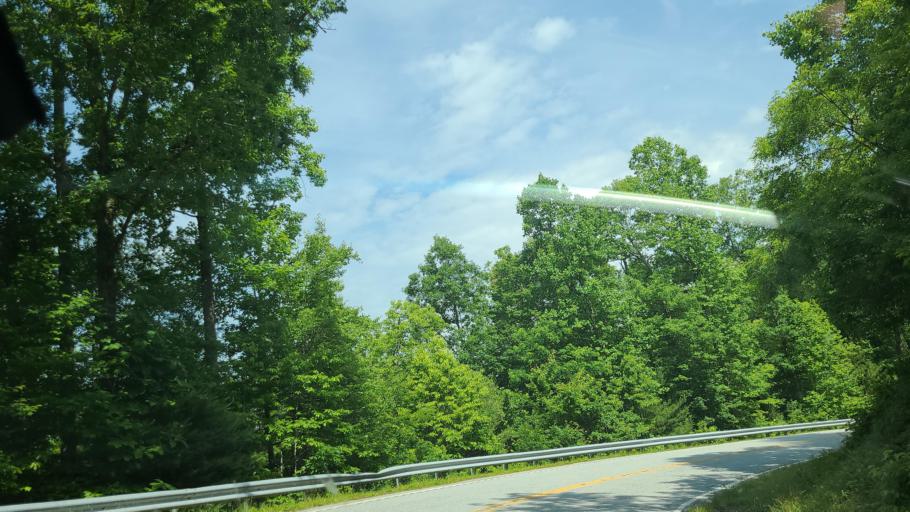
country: US
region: South Carolina
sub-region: Oconee County
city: Walhalla
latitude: 34.8967
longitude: -83.1736
